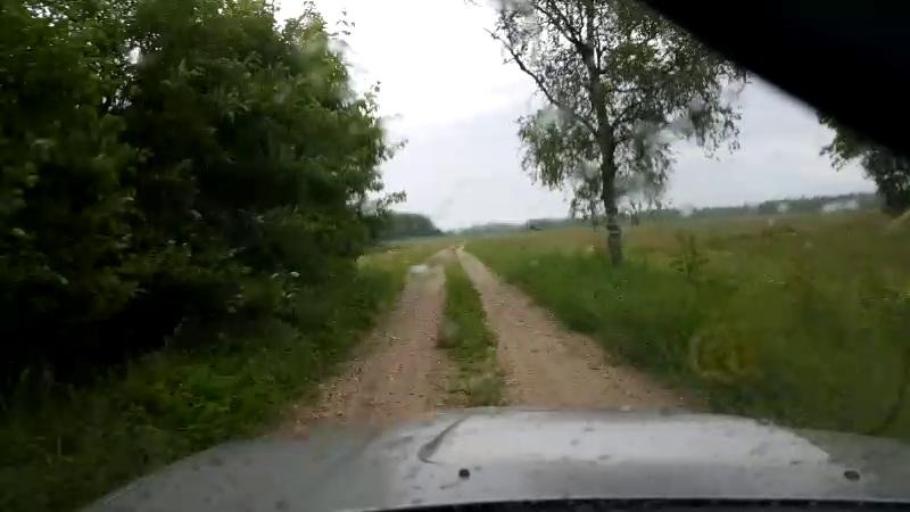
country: EE
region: Paernumaa
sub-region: Tootsi vald
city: Tootsi
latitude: 58.5866
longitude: 24.6551
